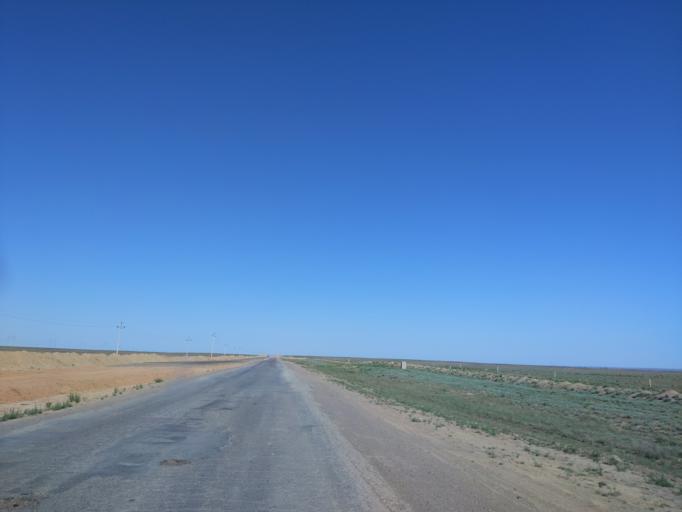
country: KZ
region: Almaty Oblysy
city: Bakanas
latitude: 44.1517
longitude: 75.8608
